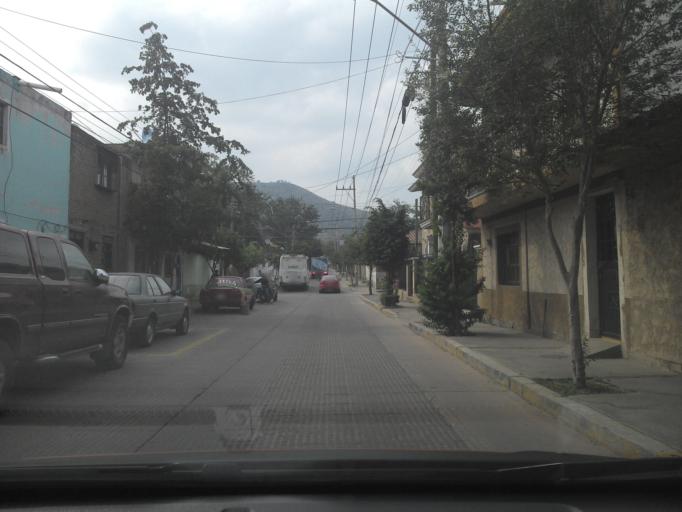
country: MX
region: Jalisco
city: Tlajomulco de Zuniga
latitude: 20.4778
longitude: -103.4491
